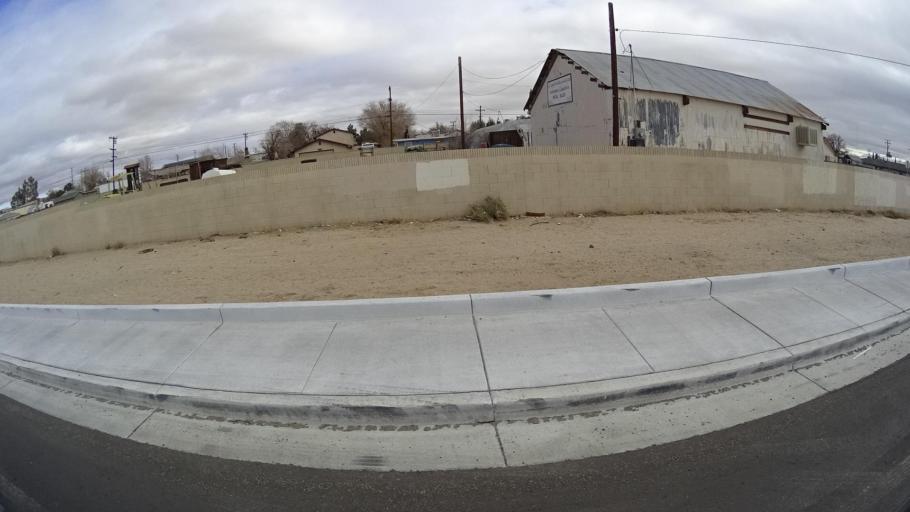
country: US
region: California
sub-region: Kern County
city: Rosamond
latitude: 34.8626
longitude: -118.1671
